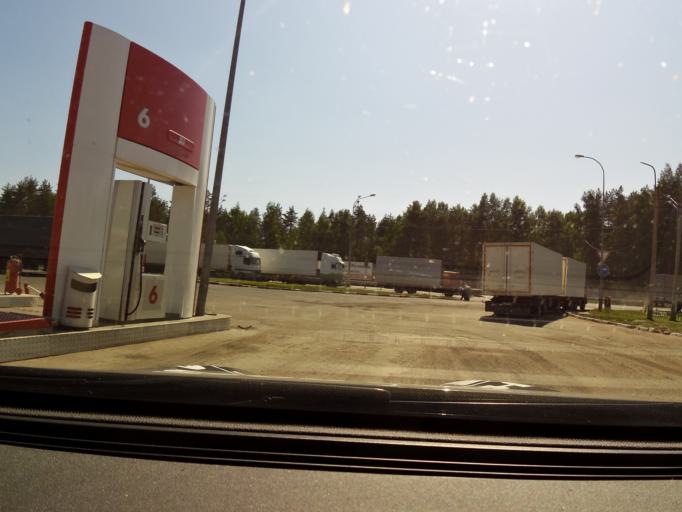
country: RU
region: Novgorod
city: Proletariy
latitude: 58.4178
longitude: 31.8393
